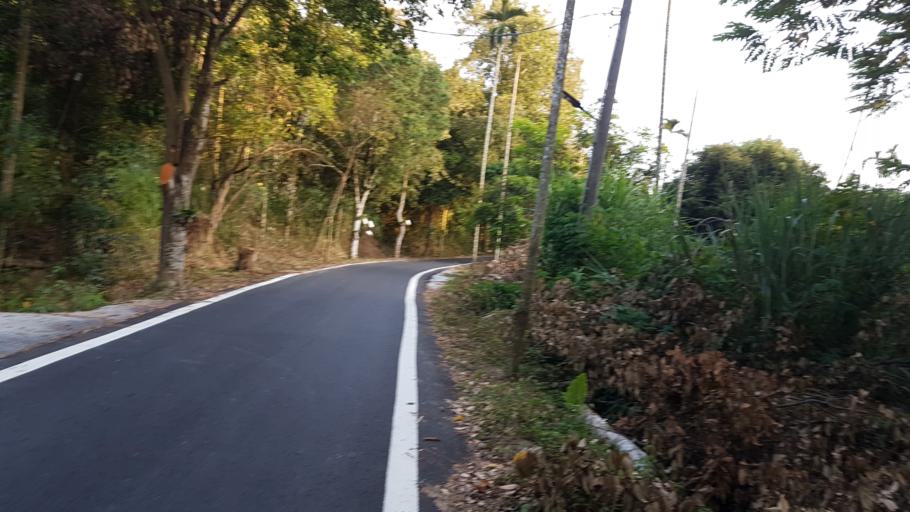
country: TW
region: Taiwan
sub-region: Chiayi
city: Jiayi Shi
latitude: 23.3632
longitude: 120.4656
